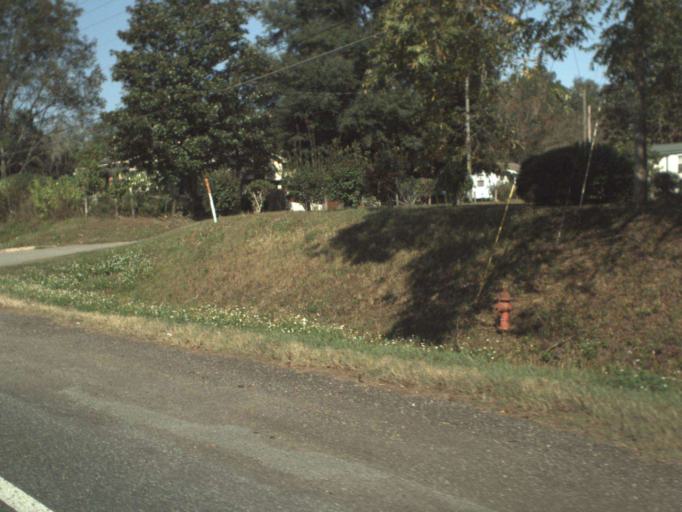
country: US
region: Florida
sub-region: Gadsden County
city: Midway
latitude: 30.4965
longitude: -84.4368
